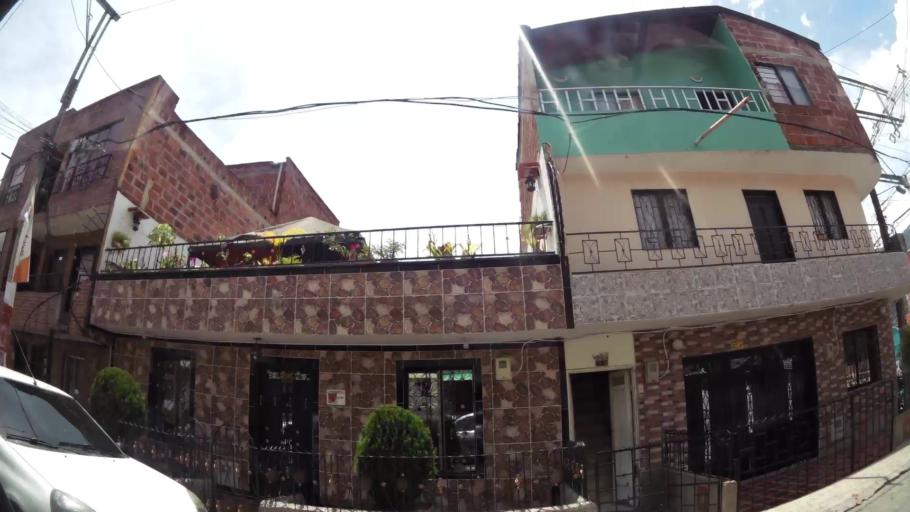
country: CO
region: Antioquia
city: Bello
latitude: 6.3479
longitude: -75.5639
